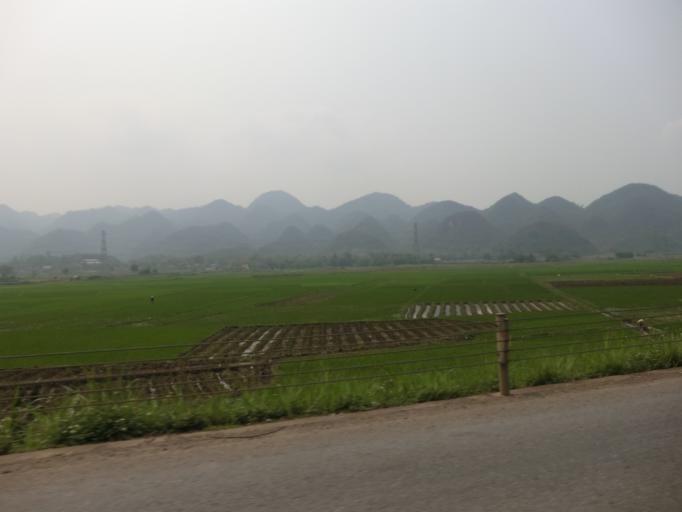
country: VN
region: Hoa Binh
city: Thi Tran Hang Tram
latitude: 20.4063
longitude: 105.5409
